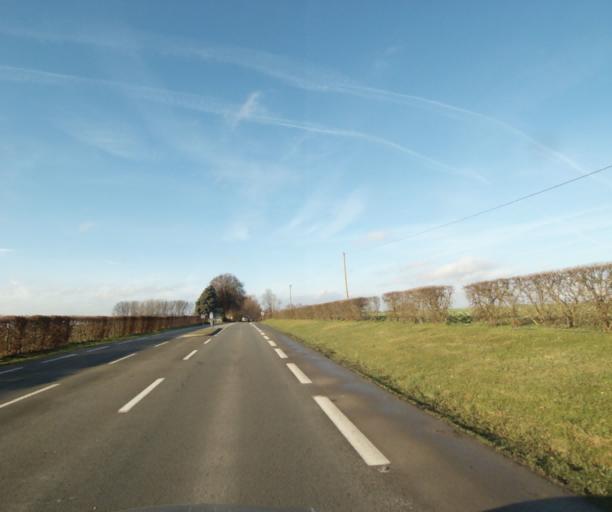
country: FR
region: Nord-Pas-de-Calais
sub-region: Departement du Nord
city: Preseau
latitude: 50.3181
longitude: 3.5687
